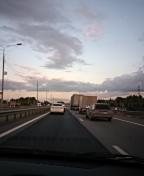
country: RU
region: Moskovskaya
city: Zhukovskiy
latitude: 55.5405
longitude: 38.0876
